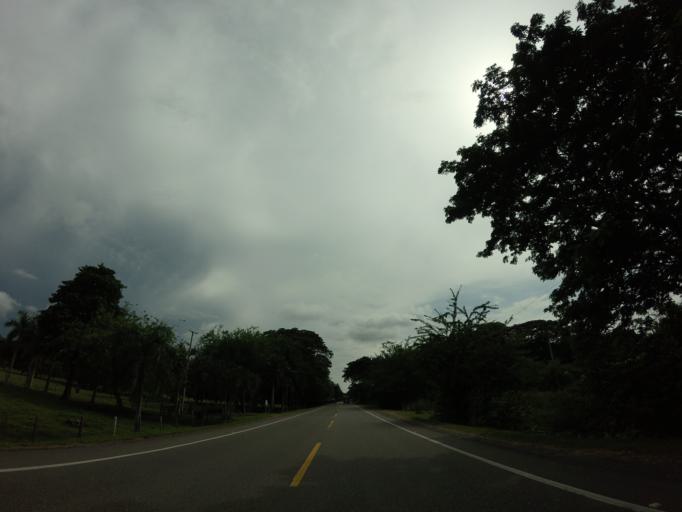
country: CO
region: Caldas
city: La Dorada
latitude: 5.4302
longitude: -74.6812
